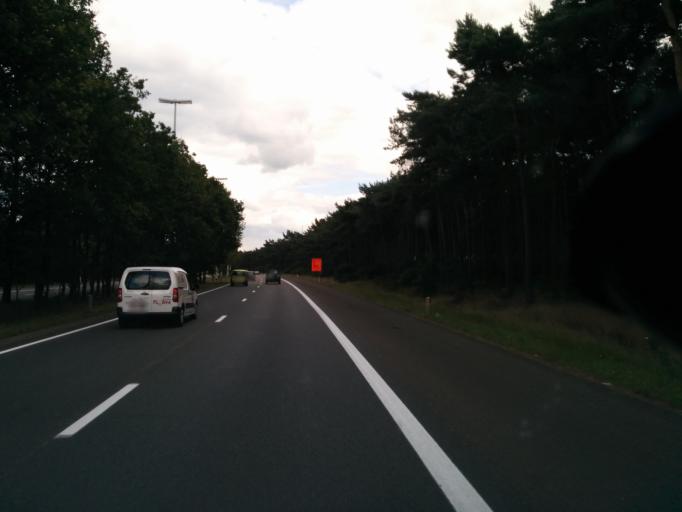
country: BE
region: Flanders
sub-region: Provincie Limburg
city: Lommel
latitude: 51.2152
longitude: 5.3482
